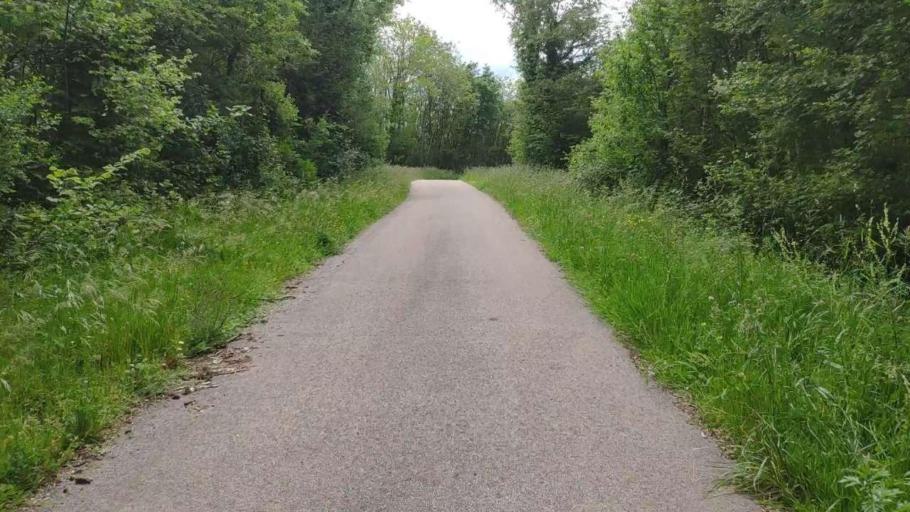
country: FR
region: Franche-Comte
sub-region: Departement du Jura
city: Perrigny
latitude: 46.7476
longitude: 5.6397
